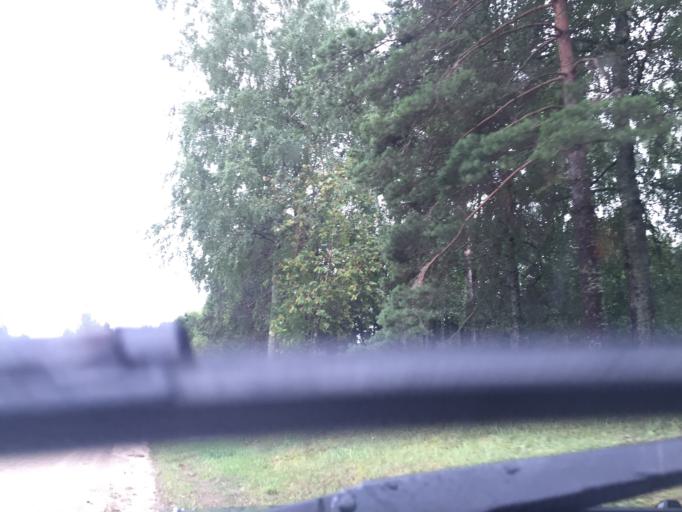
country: LV
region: Preilu Rajons
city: Jaunaglona
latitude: 56.2561
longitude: 27.2009
